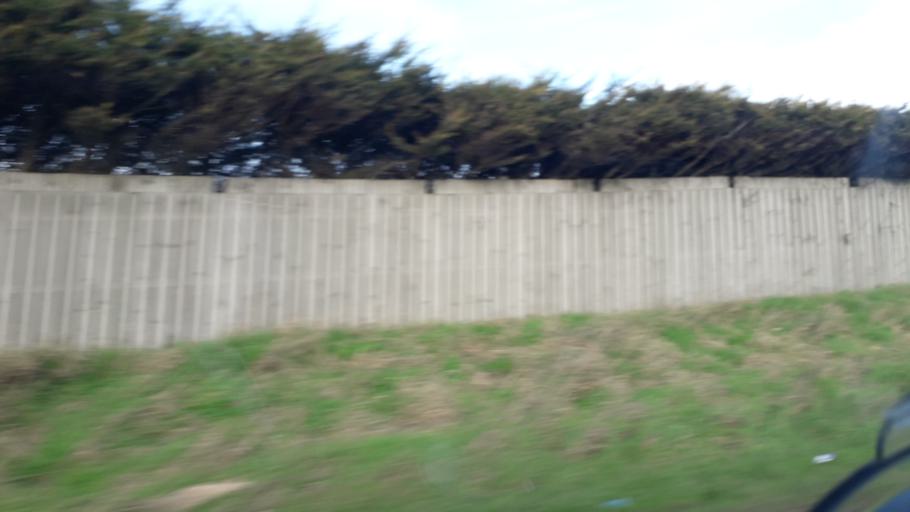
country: GB
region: Northern Ireland
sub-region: Banbridge District
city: Banbridge
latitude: 54.3348
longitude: -6.2770
